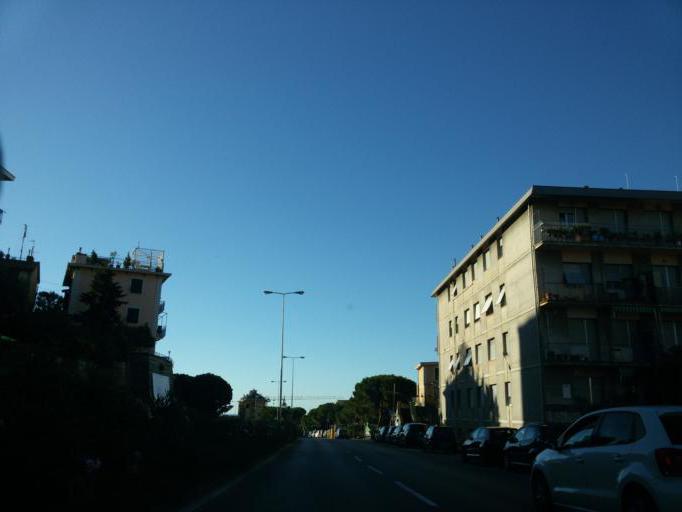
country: IT
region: Liguria
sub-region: Provincia di Genova
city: Bogliasco
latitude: 44.3912
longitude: 9.0109
